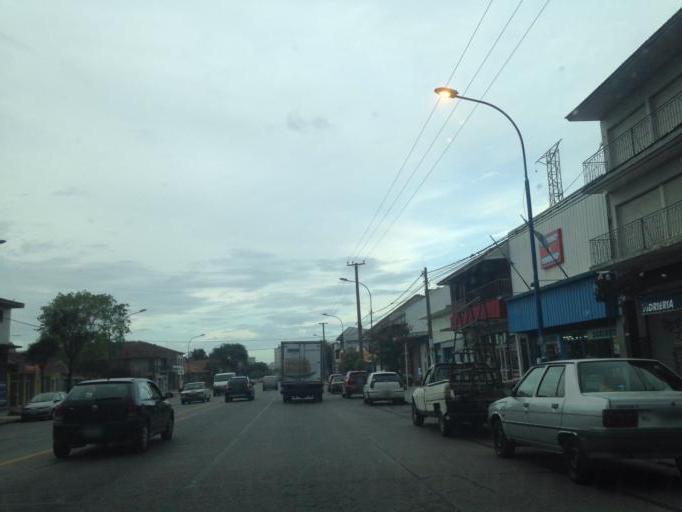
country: AR
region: Buenos Aires
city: Mar del Plata
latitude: -38.0250
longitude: -57.5783
